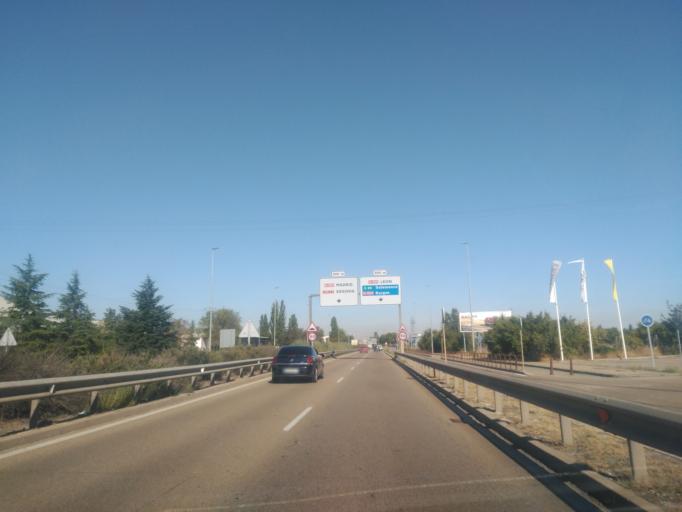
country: ES
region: Castille and Leon
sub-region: Provincia de Valladolid
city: Cisterniga
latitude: 41.6293
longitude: -4.7017
